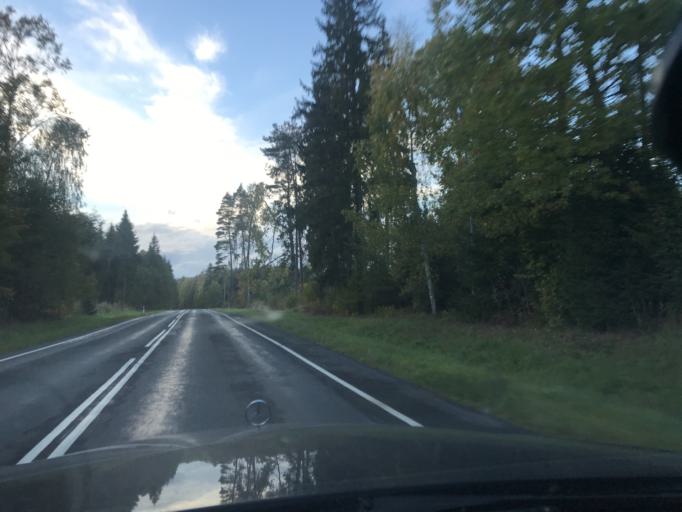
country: EE
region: Vorumaa
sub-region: Antsla vald
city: Vana-Antsla
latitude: 57.8773
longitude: 26.5833
